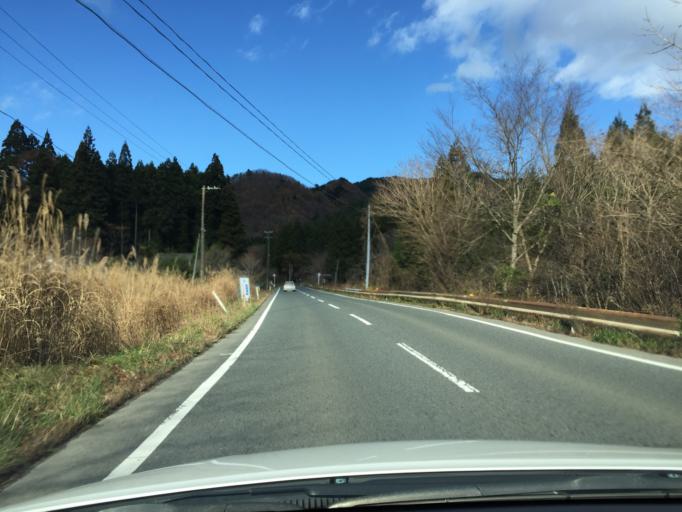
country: JP
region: Fukushima
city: Namie
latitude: 37.6826
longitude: 140.8521
